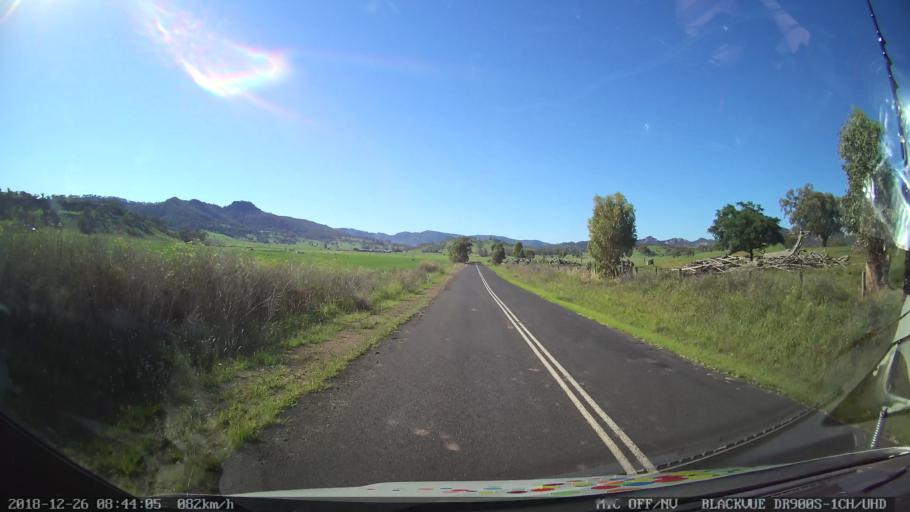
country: AU
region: New South Wales
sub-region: Mid-Western Regional
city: Kandos
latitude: -32.5101
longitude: 150.0804
